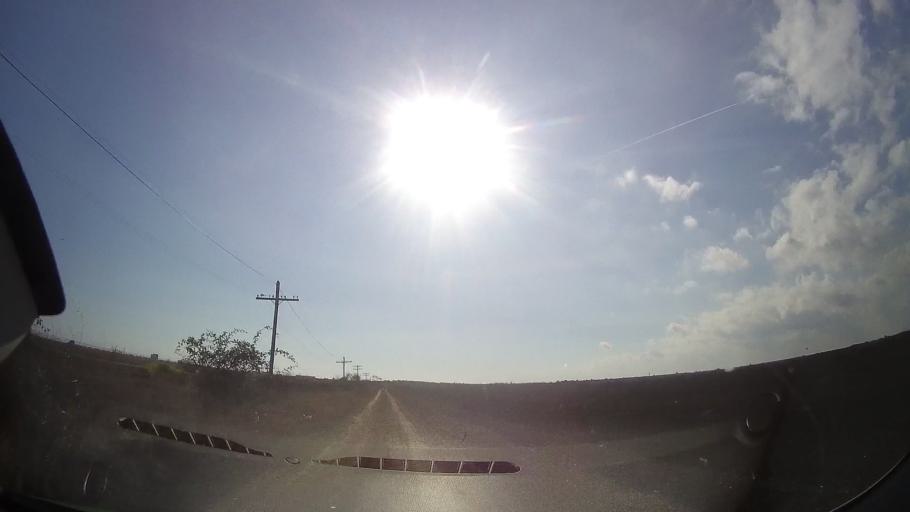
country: RO
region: Constanta
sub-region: Comuna Tuzla
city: Tuzla
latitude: 43.9826
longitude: 28.6445
